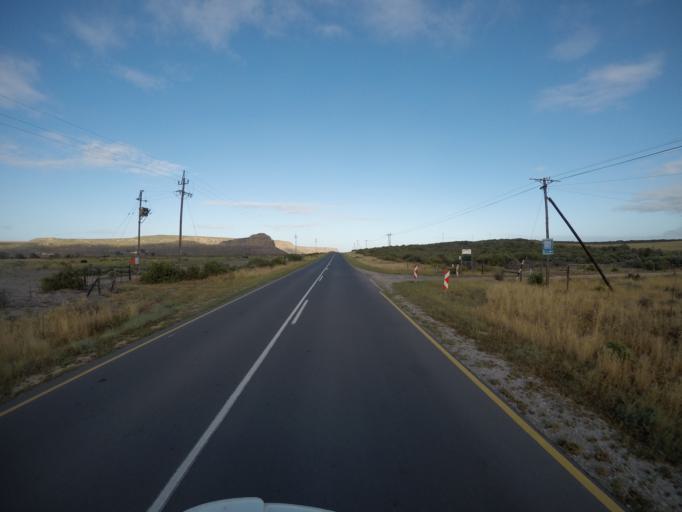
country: ZA
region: Western Cape
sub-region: West Coast District Municipality
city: Clanwilliam
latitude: -32.3124
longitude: 18.3700
